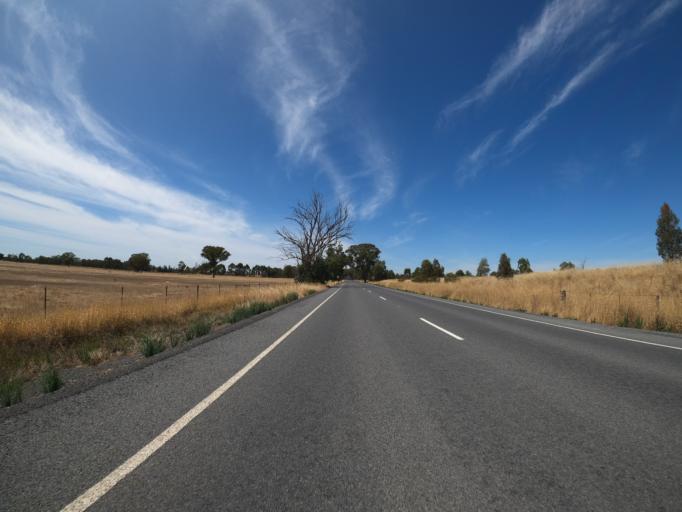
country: AU
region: Victoria
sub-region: Benalla
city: Benalla
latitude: -36.5203
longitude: 146.0348
